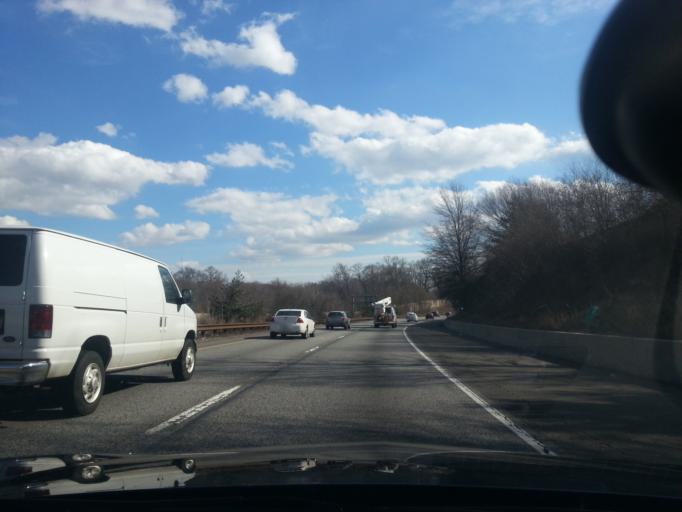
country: US
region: Pennsylvania
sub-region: Delaware County
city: Swarthmore
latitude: 39.8978
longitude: -75.3598
